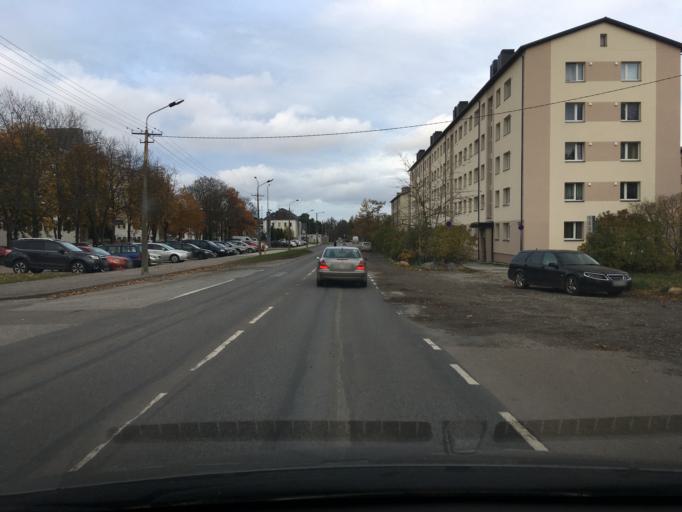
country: EE
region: Harju
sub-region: Tallinna linn
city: Tallinn
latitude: 59.3954
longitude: 24.7093
